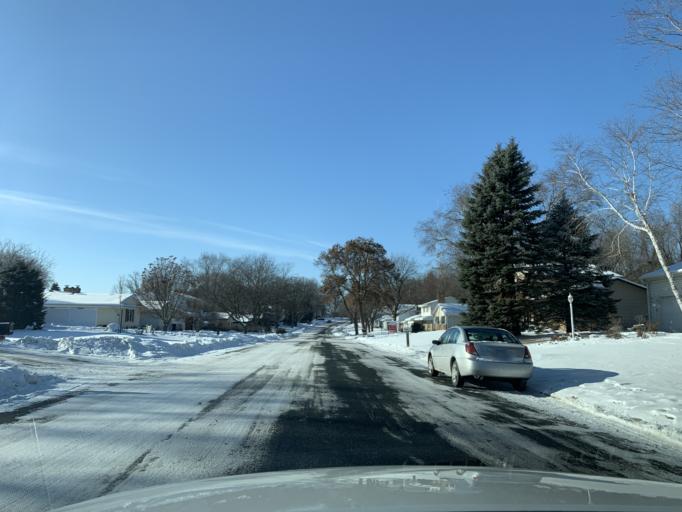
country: US
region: Minnesota
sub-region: Scott County
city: Savage
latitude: 44.8202
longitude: -93.3396
